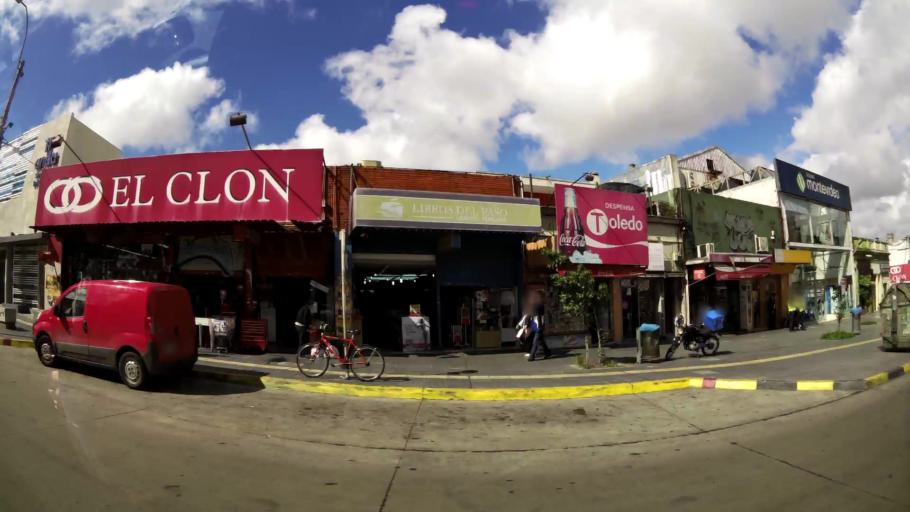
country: UY
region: Montevideo
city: Montevideo
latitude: -34.8575
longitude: -56.2185
